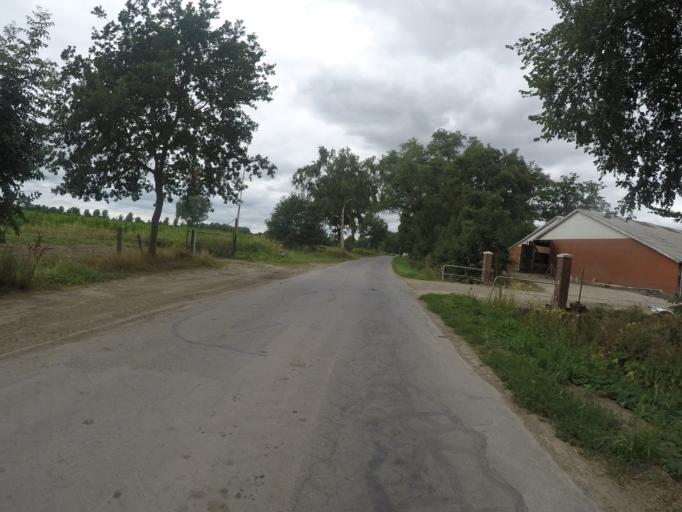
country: DE
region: Lower Saxony
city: Grossenworden
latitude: 53.6815
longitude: 9.2446
